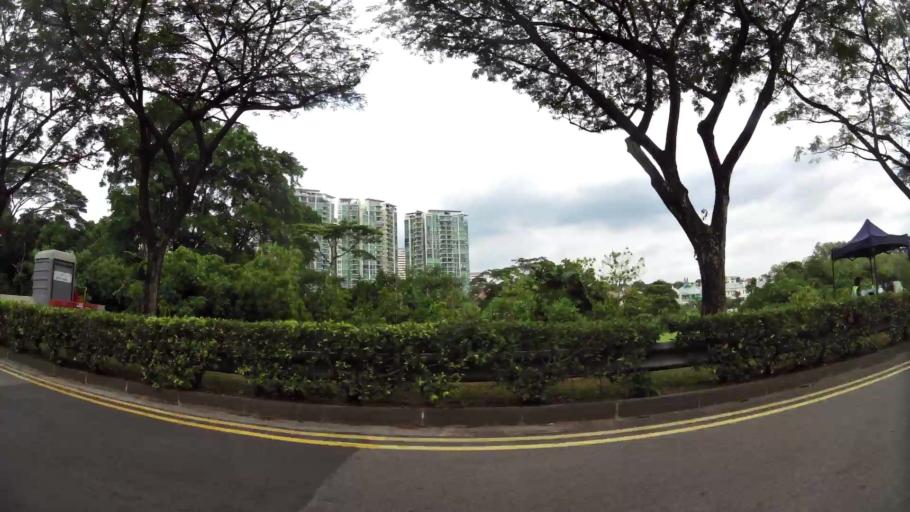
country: SG
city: Singapore
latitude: 1.3121
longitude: 103.7778
